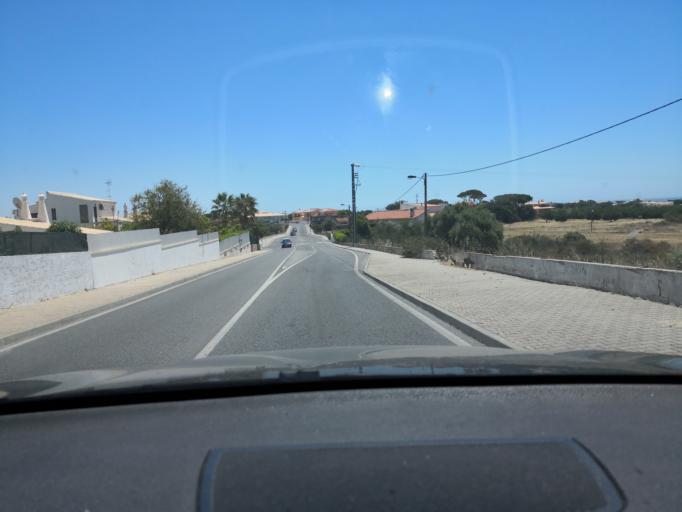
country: PT
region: Faro
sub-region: Albufeira
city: Ferreiras
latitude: 37.1059
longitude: -8.1994
